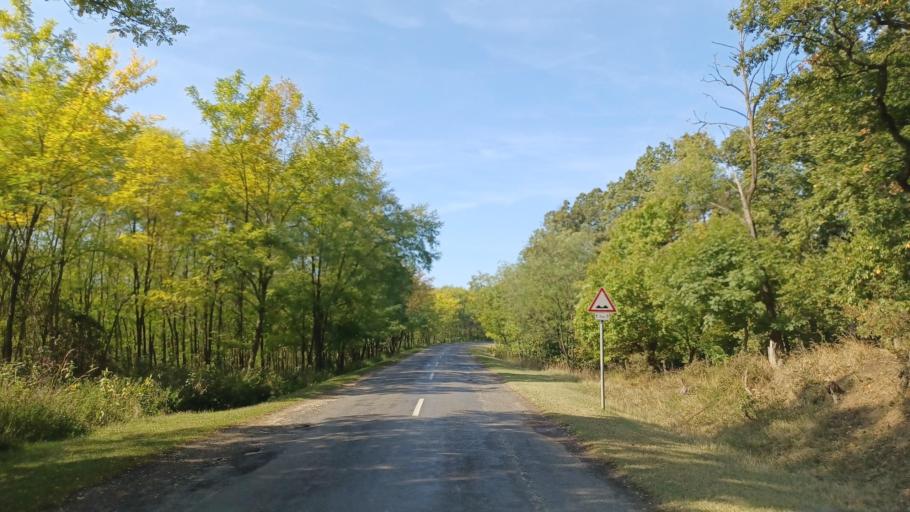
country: HU
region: Tolna
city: Pincehely
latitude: 46.6639
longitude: 18.4895
